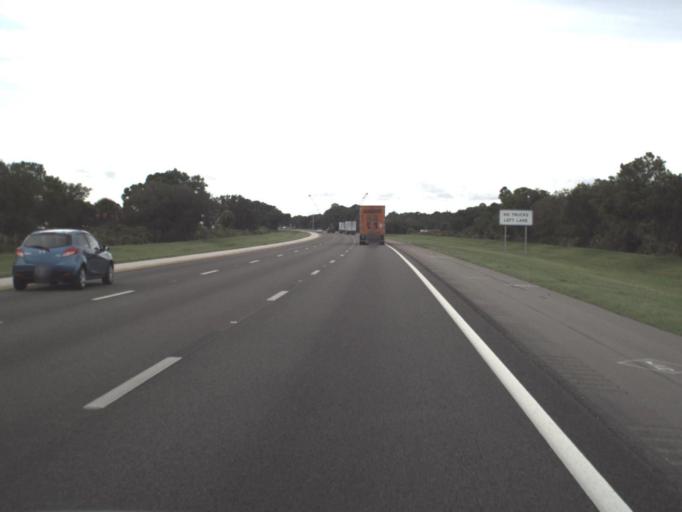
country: US
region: Florida
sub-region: Sarasota County
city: Laurel
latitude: 27.1709
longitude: -82.4338
